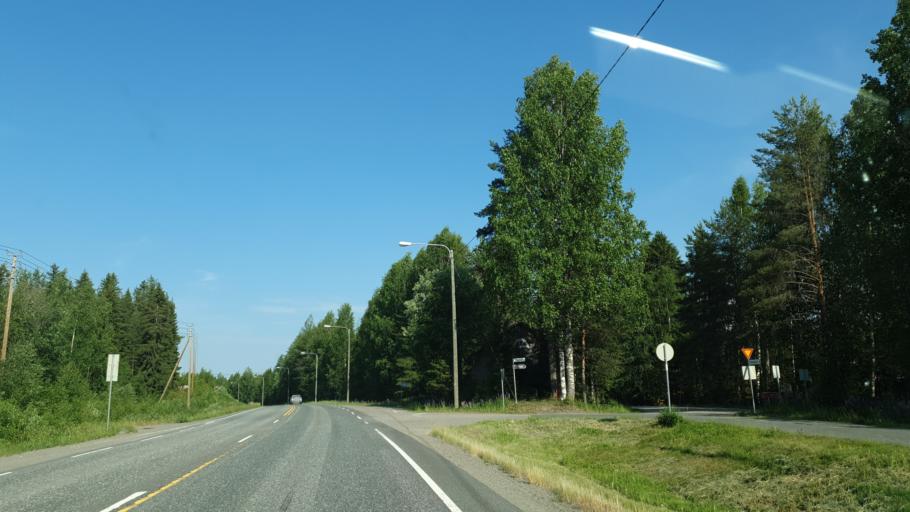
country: FI
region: Northern Savo
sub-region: Kuopio
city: Siilinjaervi
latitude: 63.1332
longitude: 27.8135
